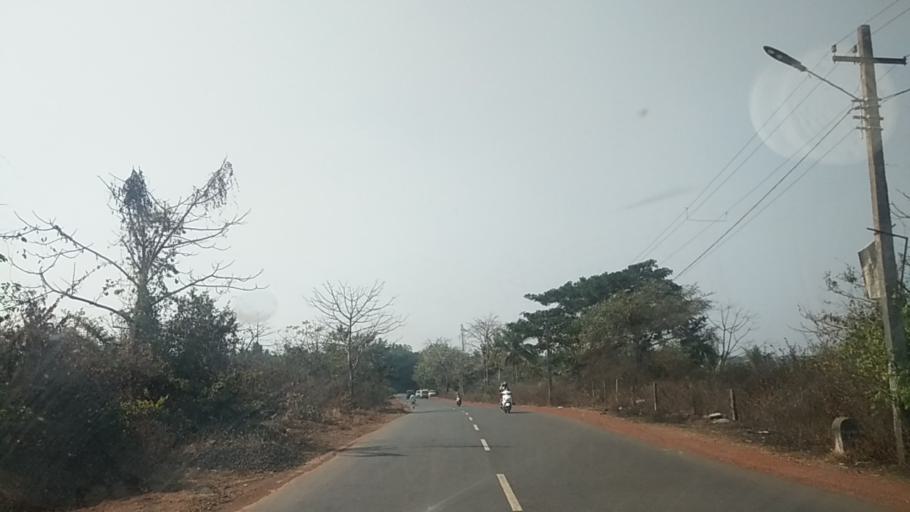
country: IN
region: Goa
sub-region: North Goa
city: Dicholi
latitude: 15.5830
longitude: 73.9640
